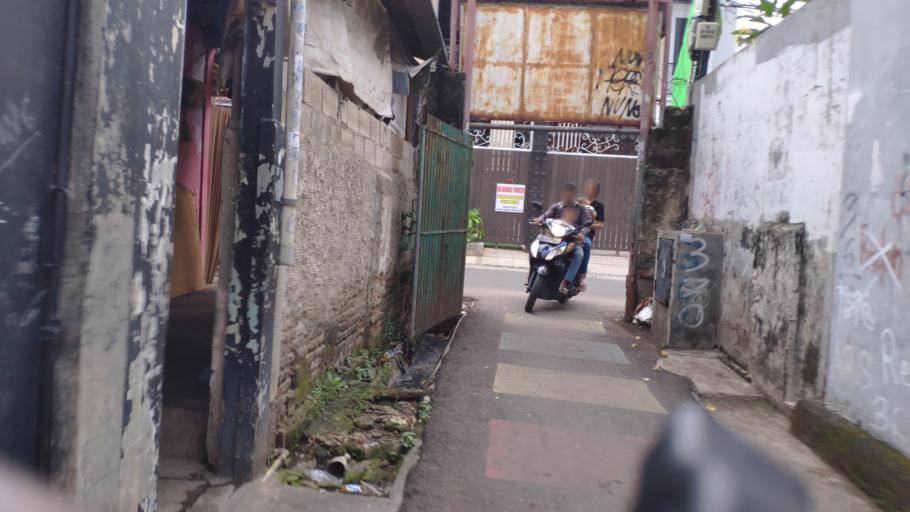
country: ID
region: Jakarta Raya
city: Jakarta
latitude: -6.2141
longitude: 106.8398
